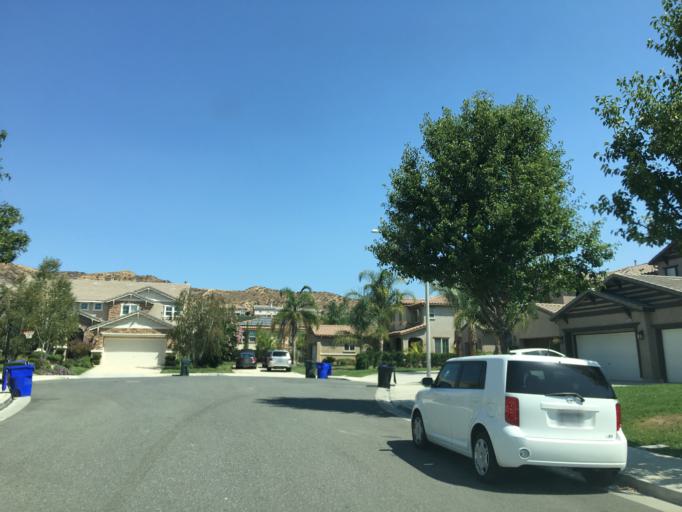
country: US
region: California
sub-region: Los Angeles County
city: Valencia
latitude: 34.4716
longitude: -118.5635
